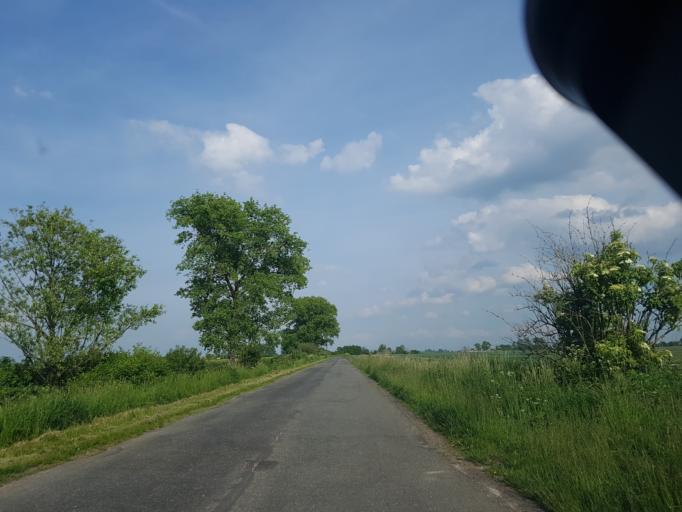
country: PL
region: Lower Silesian Voivodeship
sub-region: Powiat strzelinski
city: Wiazow
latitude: 50.8655
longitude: 17.1623
